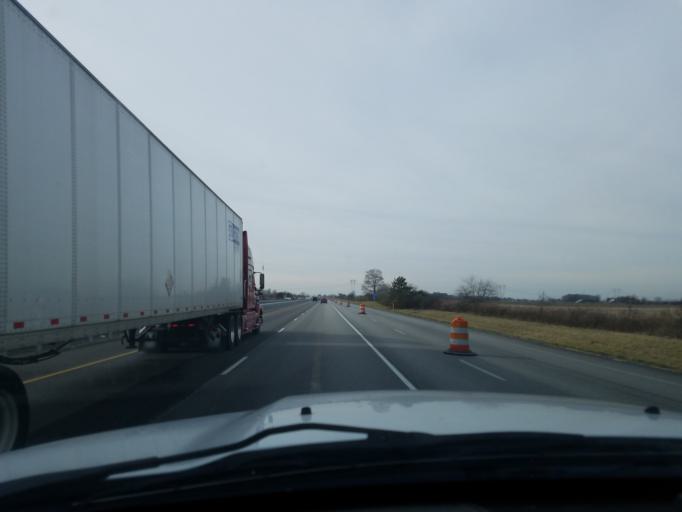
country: US
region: Indiana
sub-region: Madison County
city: Ingalls
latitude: 39.9918
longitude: -85.8016
